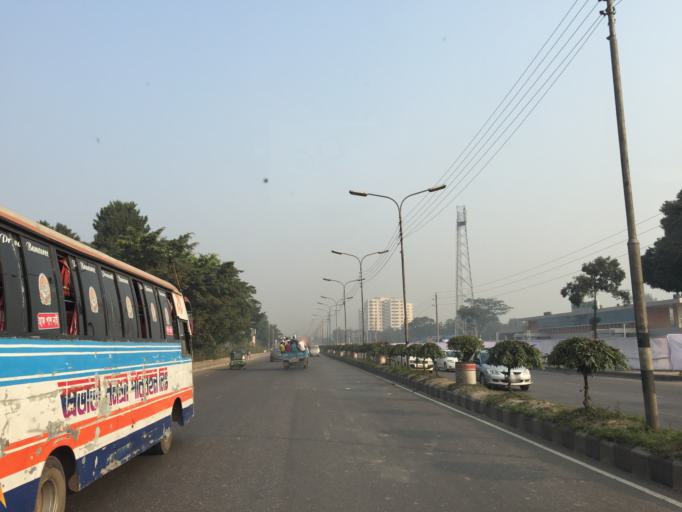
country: BD
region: Dhaka
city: Paltan
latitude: 23.8046
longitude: 90.4026
